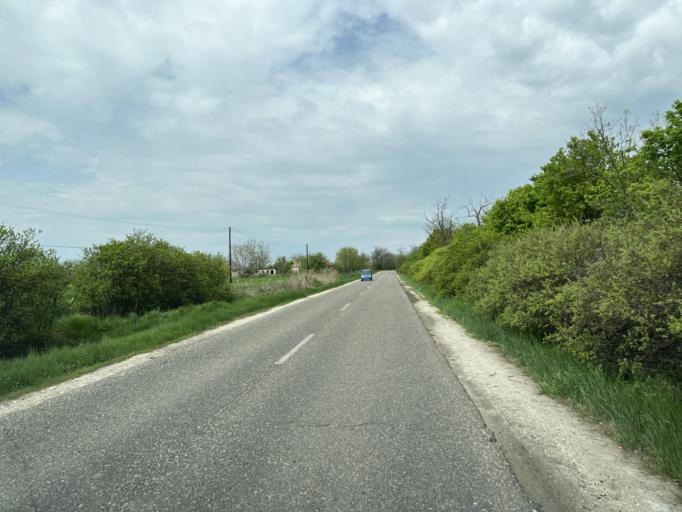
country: HU
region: Pest
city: Tortel
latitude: 47.1287
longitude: 19.9205
